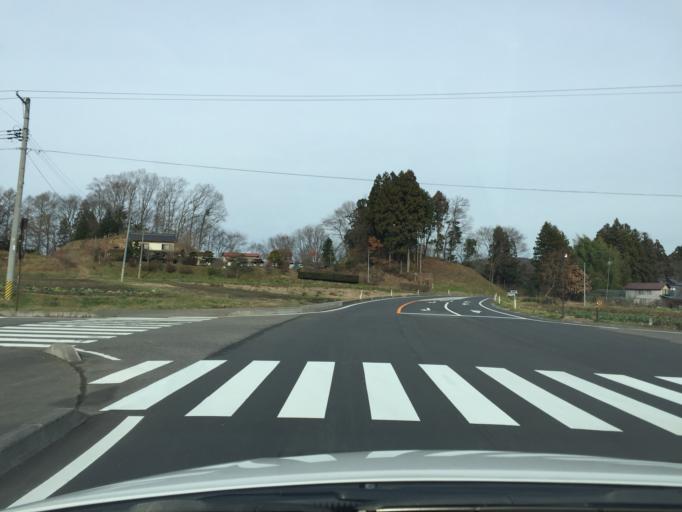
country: JP
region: Fukushima
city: Funehikimachi-funehiki
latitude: 37.3581
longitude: 140.6048
